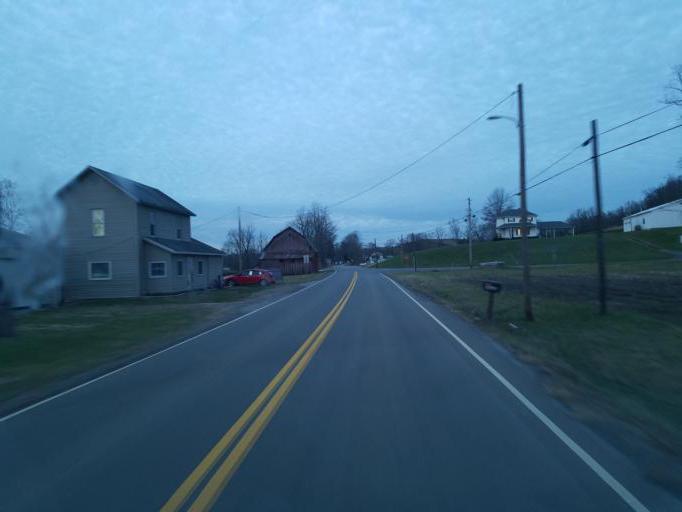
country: US
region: Ohio
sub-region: Muskingum County
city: Dresden
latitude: 40.1956
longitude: -82.0448
